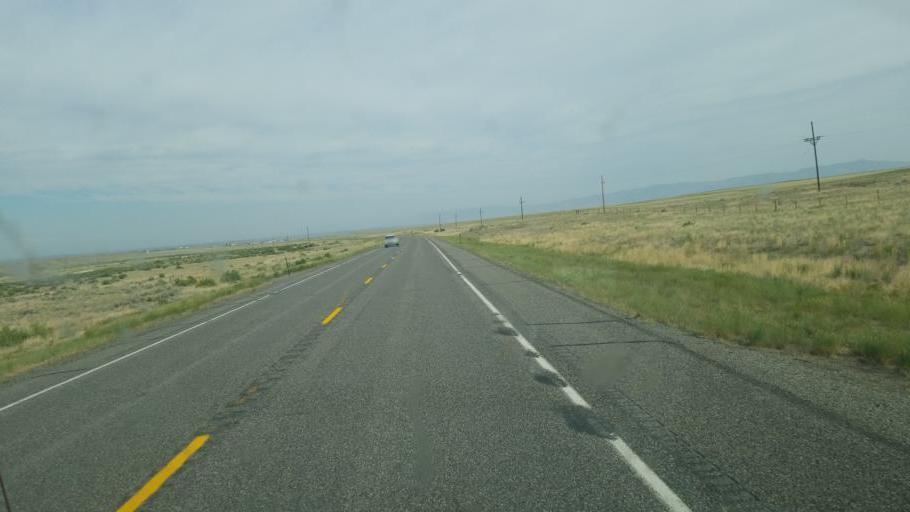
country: US
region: Wyoming
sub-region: Fremont County
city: Riverton
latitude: 43.2307
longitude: -108.0610
